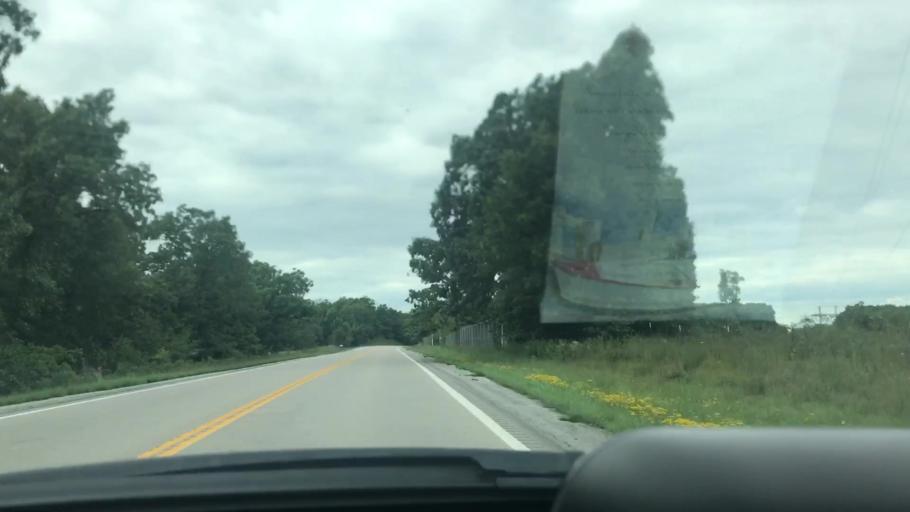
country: US
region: Missouri
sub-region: Benton County
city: Warsaw
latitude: 38.1637
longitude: -93.3053
